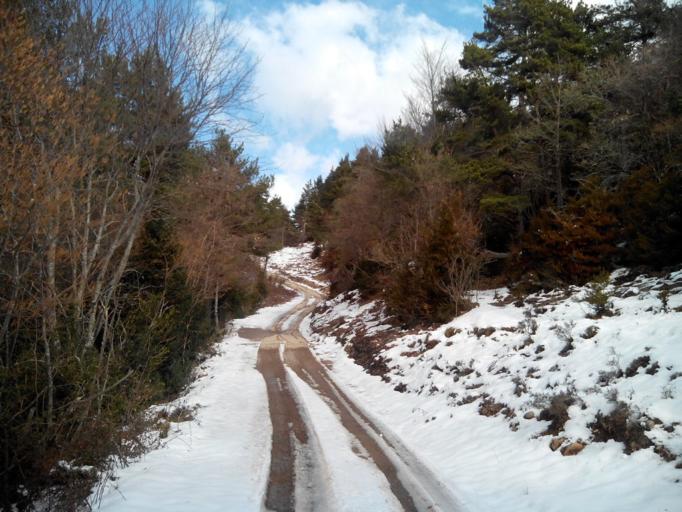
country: ES
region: Catalonia
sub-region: Provincia de Barcelona
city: Sant Julia de Cerdanyola
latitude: 42.1875
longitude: 1.9280
